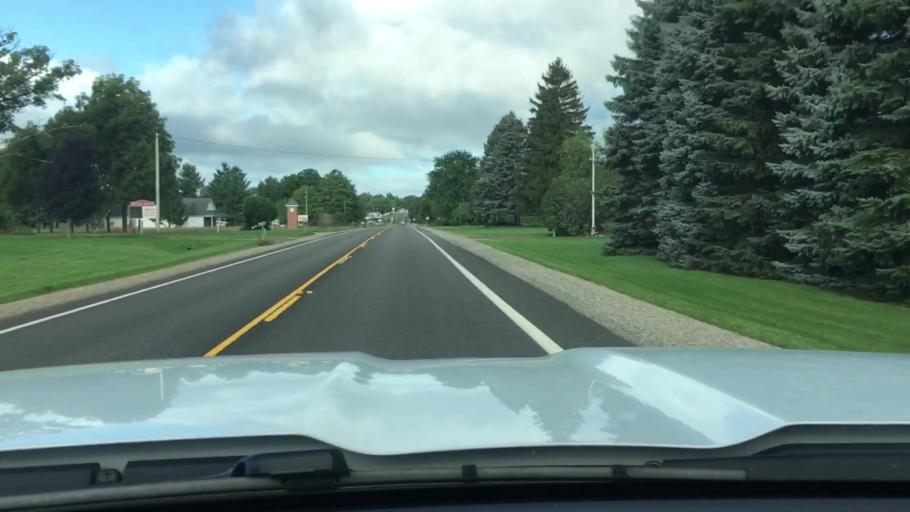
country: US
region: Michigan
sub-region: Lapeer County
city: Barnes Lake-Millers Lake
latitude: 43.3379
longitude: -83.3331
